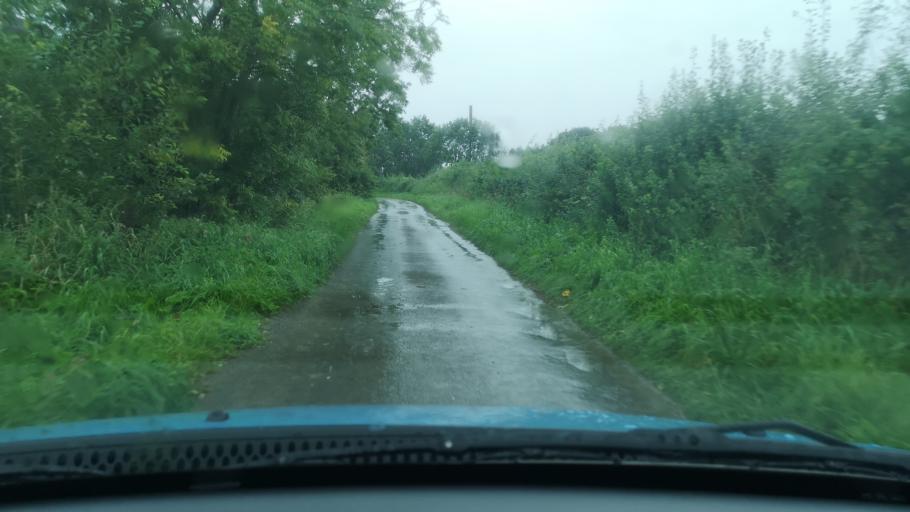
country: GB
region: England
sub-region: City and Borough of Wakefield
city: Low Ackworth
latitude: 53.6662
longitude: -1.3229
